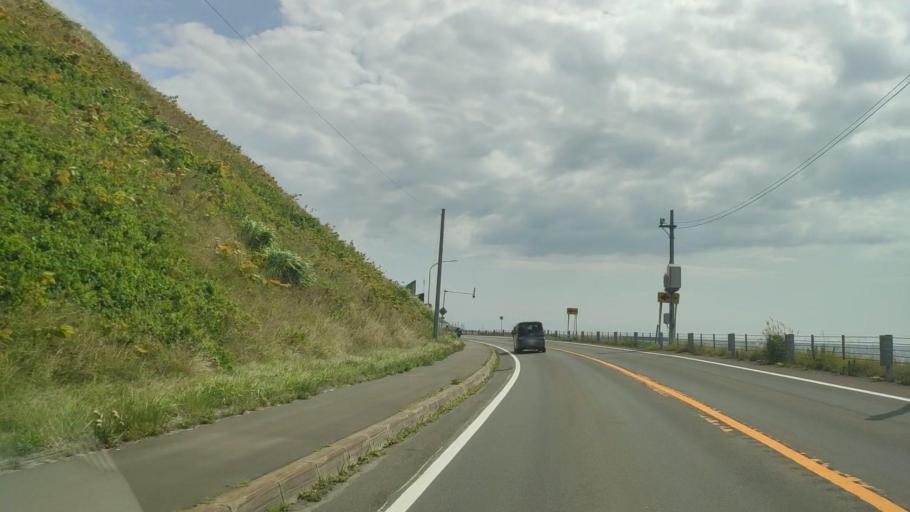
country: JP
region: Hokkaido
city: Rumoi
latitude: 44.2339
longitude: 141.6565
